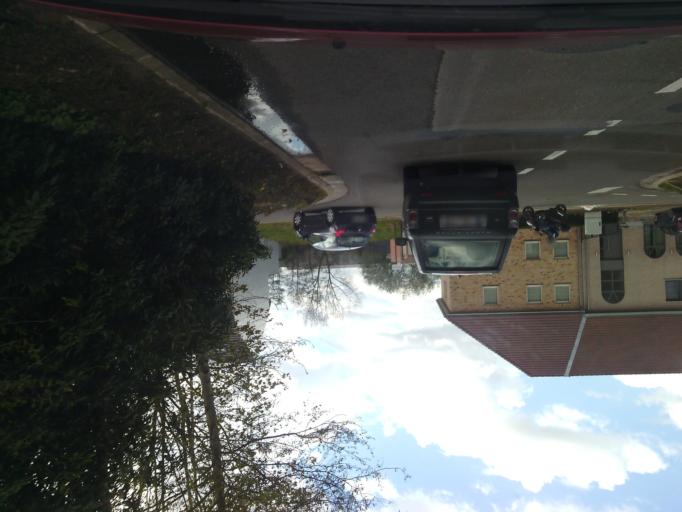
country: BE
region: Flanders
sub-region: Provincie Oost-Vlaanderen
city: Sint-Niklaas
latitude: 51.1461
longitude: 4.1738
